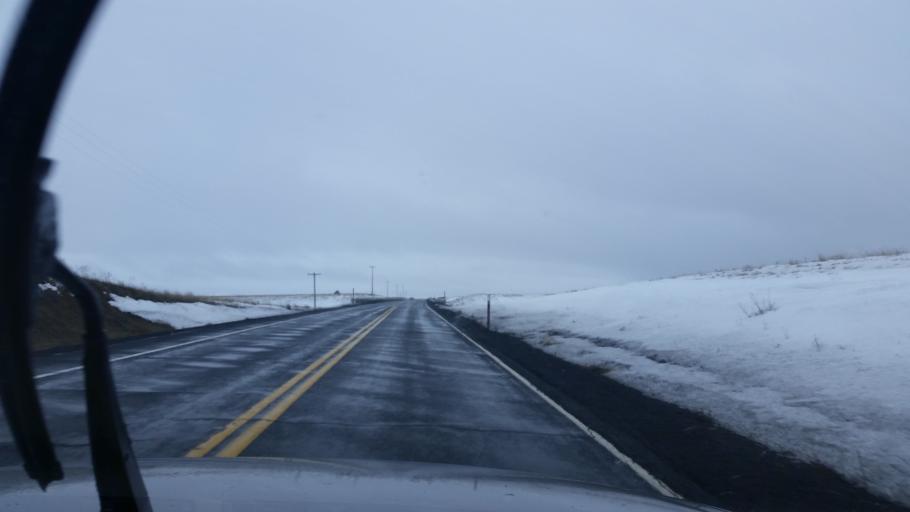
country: US
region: Washington
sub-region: Lincoln County
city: Davenport
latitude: 47.4783
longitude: -118.2174
